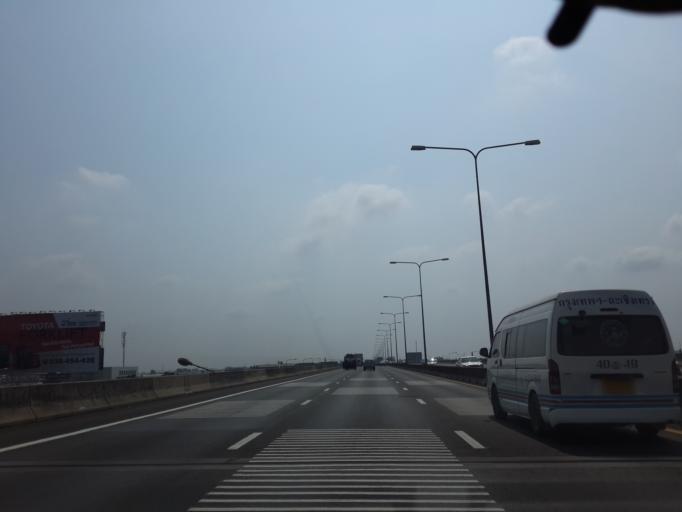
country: TH
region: Samut Prakan
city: Bang Bo District
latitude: 13.6224
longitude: 100.7345
